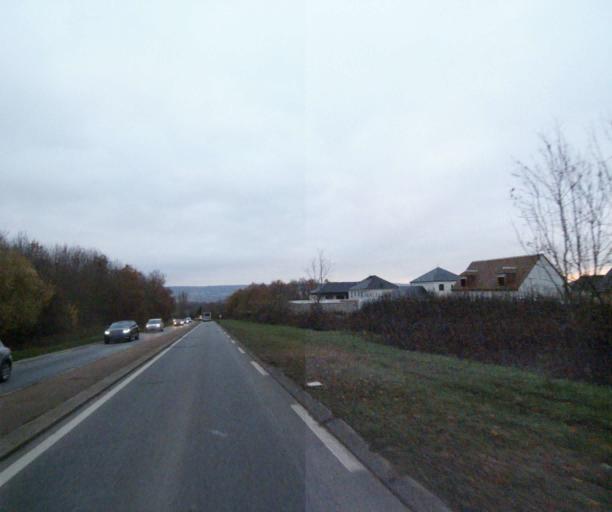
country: FR
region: Ile-de-France
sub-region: Departement des Yvelines
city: Medan
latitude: 48.9530
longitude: 1.9795
